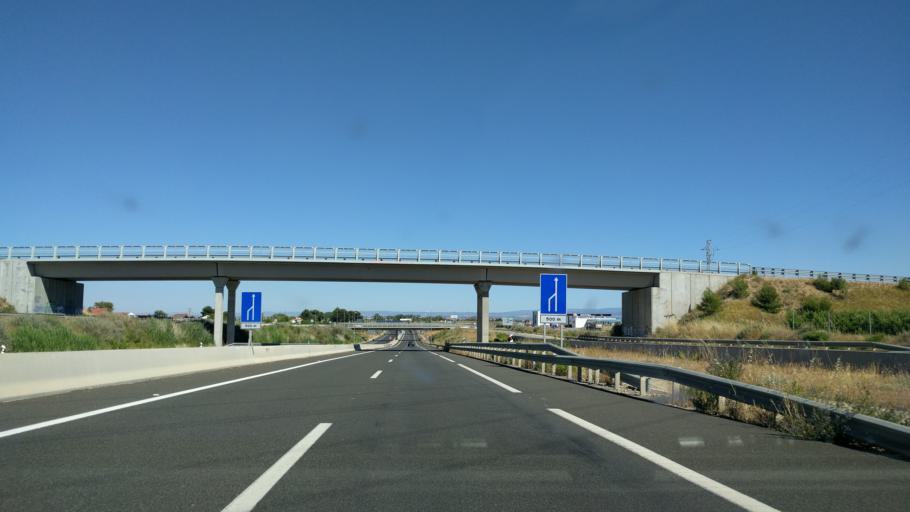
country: ES
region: Catalonia
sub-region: Provincia de Lleida
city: Alpicat
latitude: 41.6501
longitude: 0.5560
